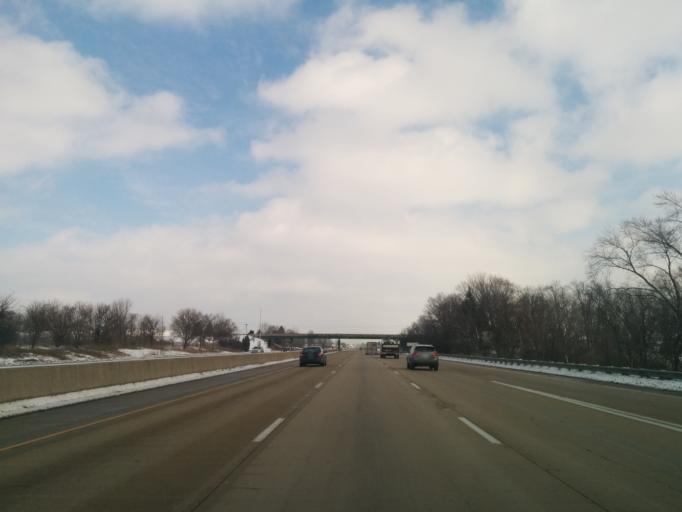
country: US
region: Illinois
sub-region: Will County
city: Mokena
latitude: 41.5523
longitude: -87.8930
